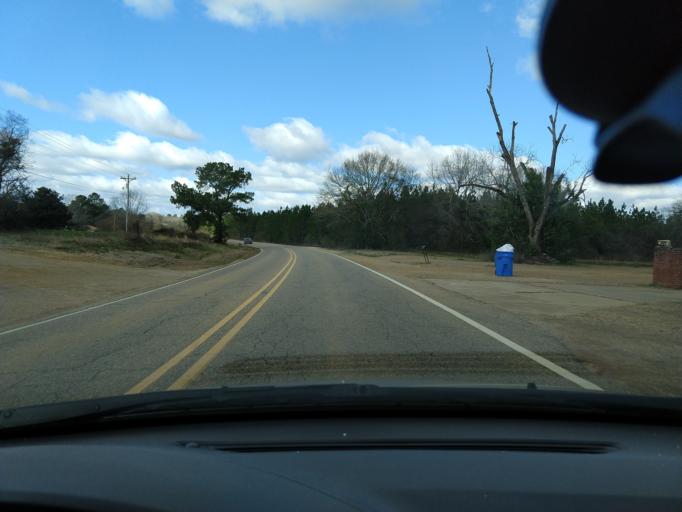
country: US
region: Alabama
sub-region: Coffee County
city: New Brockton
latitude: 31.3161
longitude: -85.9347
